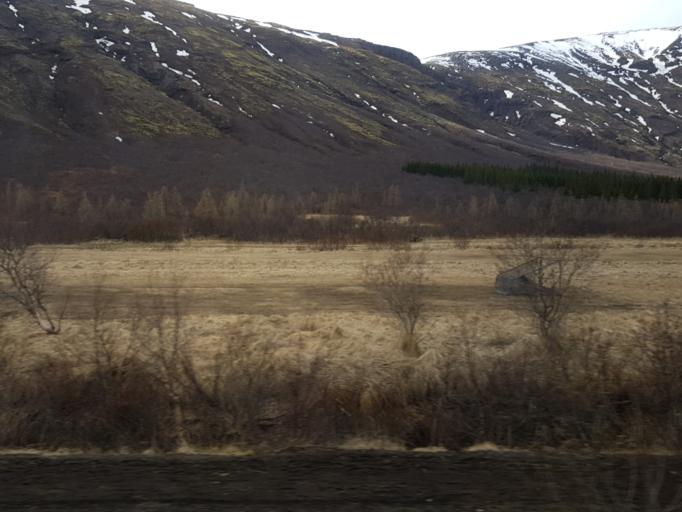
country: IS
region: South
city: Selfoss
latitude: 64.2225
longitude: -20.7277
